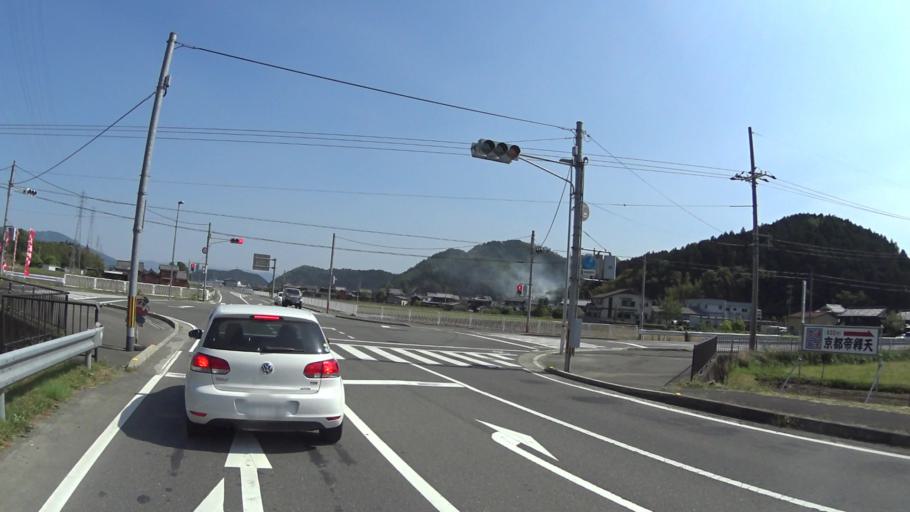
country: JP
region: Kyoto
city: Kameoka
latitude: 35.1046
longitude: 135.5267
